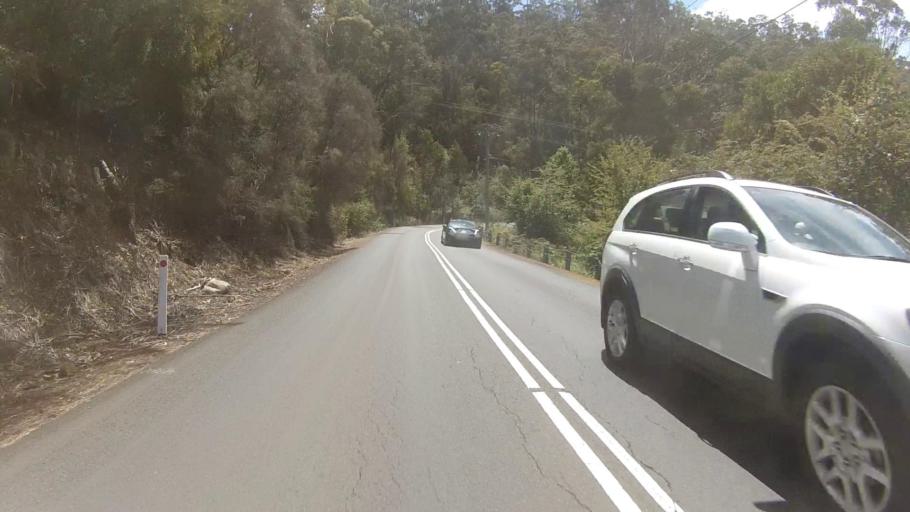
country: AU
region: Tasmania
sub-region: Kingborough
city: Taroona
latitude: -42.9603
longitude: 147.3314
